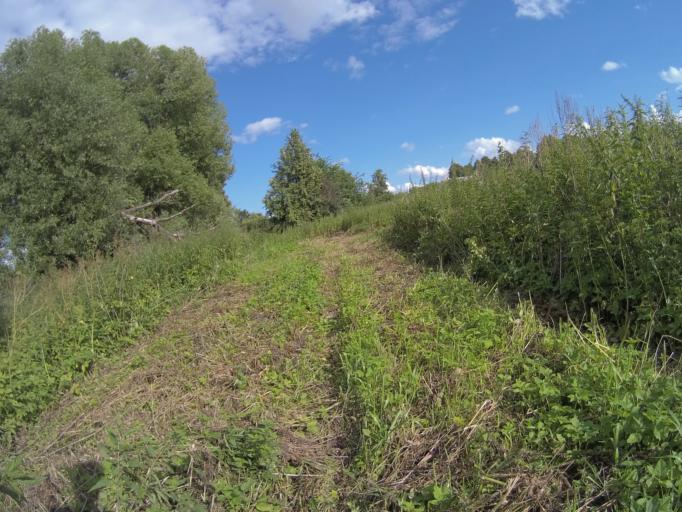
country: RU
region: Vladimir
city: Suzdal'
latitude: 56.2978
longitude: 40.3606
